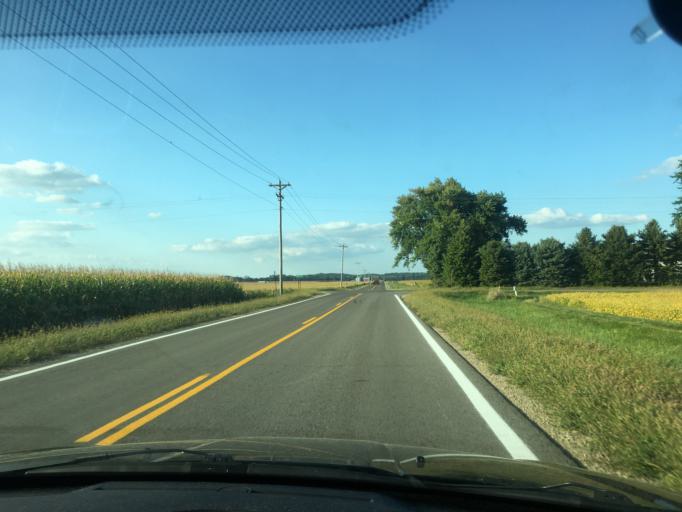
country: US
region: Ohio
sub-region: Logan County
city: West Liberty
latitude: 40.1931
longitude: -83.7811
